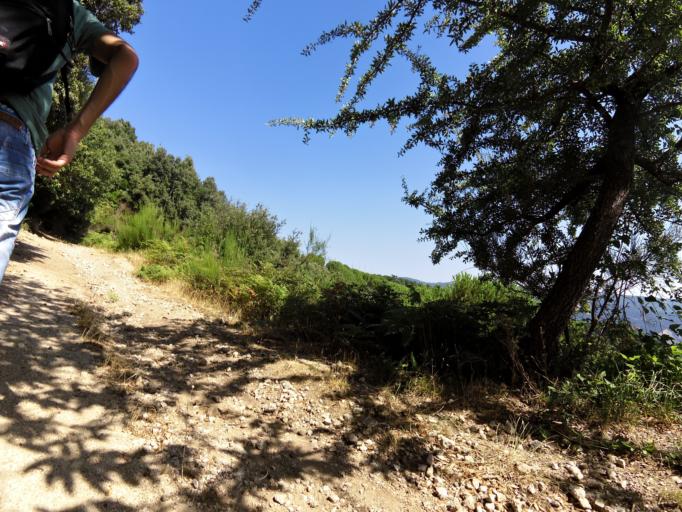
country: IT
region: Calabria
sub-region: Provincia di Reggio Calabria
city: Bivongi
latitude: 38.5069
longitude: 16.4364
